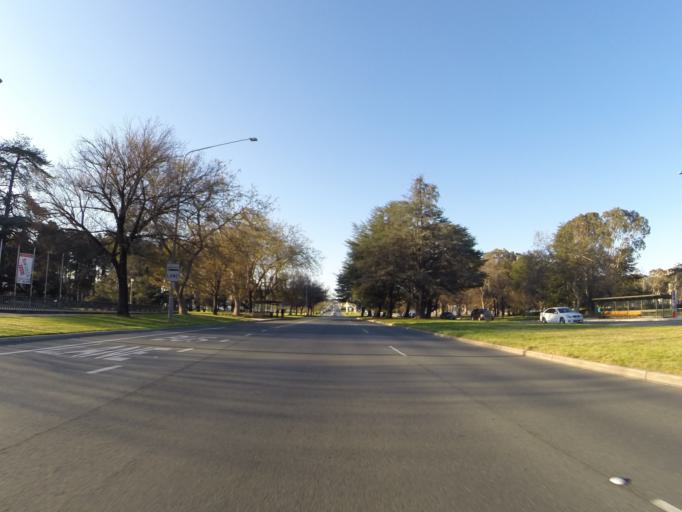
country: AU
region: Australian Capital Territory
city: Canberra
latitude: -35.2984
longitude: 149.1259
